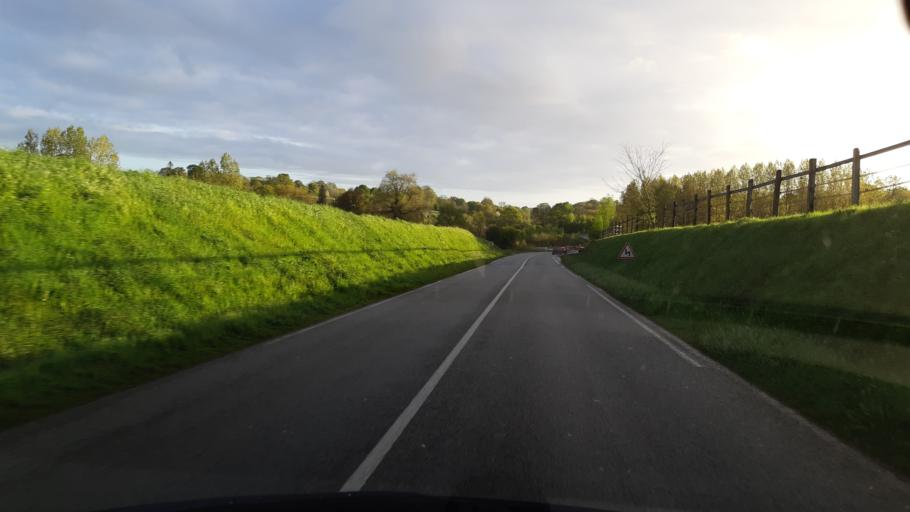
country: FR
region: Lower Normandy
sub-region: Departement de la Manche
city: Agneaux
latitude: 49.0671
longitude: -1.1314
